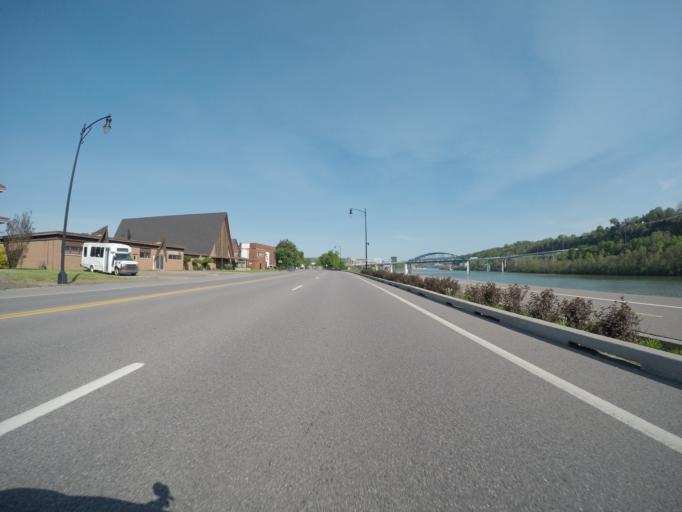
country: US
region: West Virginia
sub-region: Kanawha County
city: Charleston
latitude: 38.3598
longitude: -81.6543
